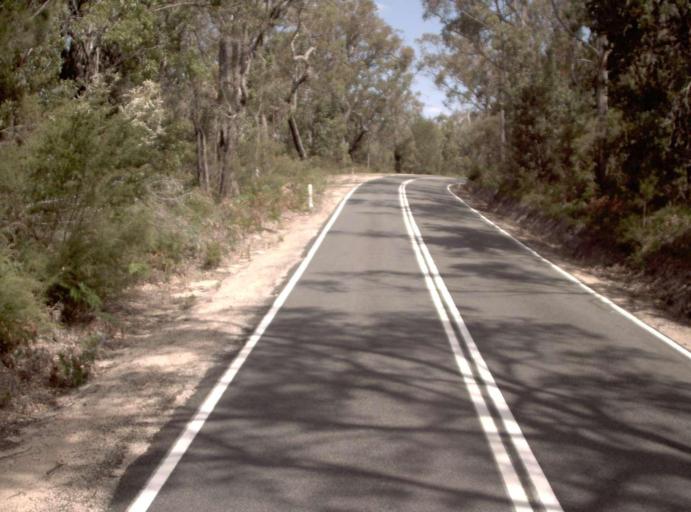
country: AU
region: New South Wales
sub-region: Bega Valley
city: Eden
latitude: -37.4904
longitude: 149.6621
